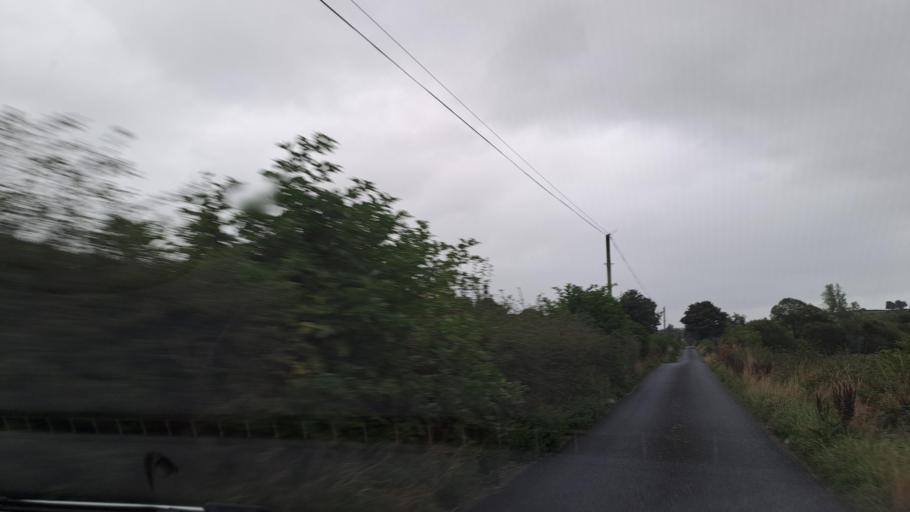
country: IE
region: Ulster
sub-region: An Cabhan
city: Kingscourt
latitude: 54.0003
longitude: -6.8472
